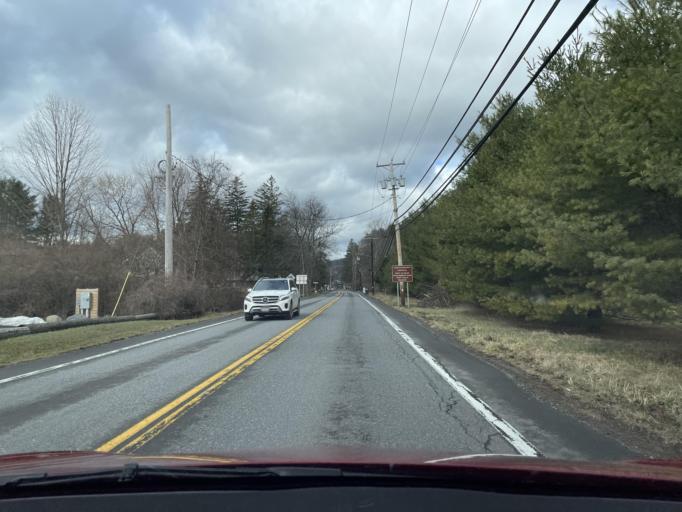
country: US
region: New York
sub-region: Ulster County
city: Woodstock
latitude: 42.0405
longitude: -74.1476
